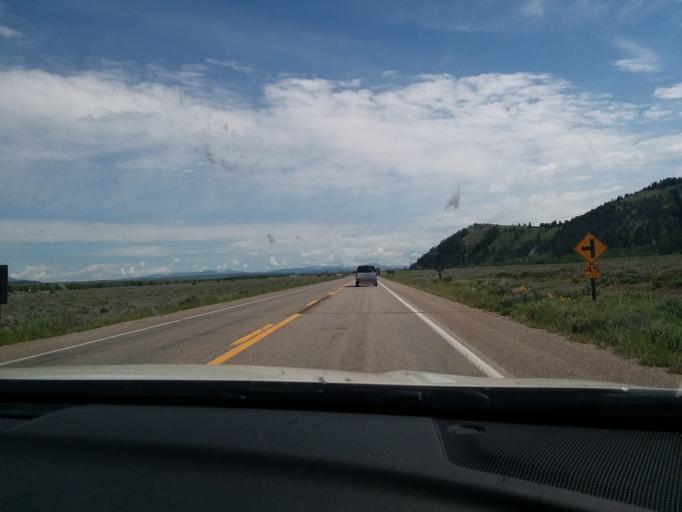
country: US
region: Wyoming
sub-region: Teton County
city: Jackson
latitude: 43.6477
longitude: -110.7099
